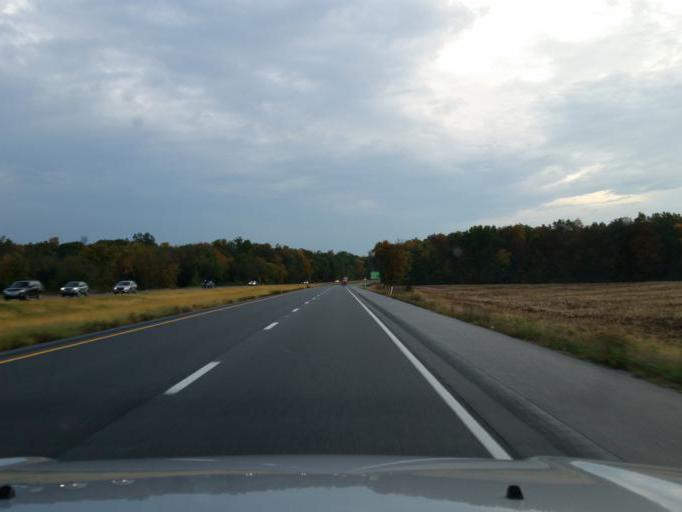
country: US
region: Pennsylvania
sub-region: Adams County
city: Biglerville
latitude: 39.9094
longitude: -77.1665
